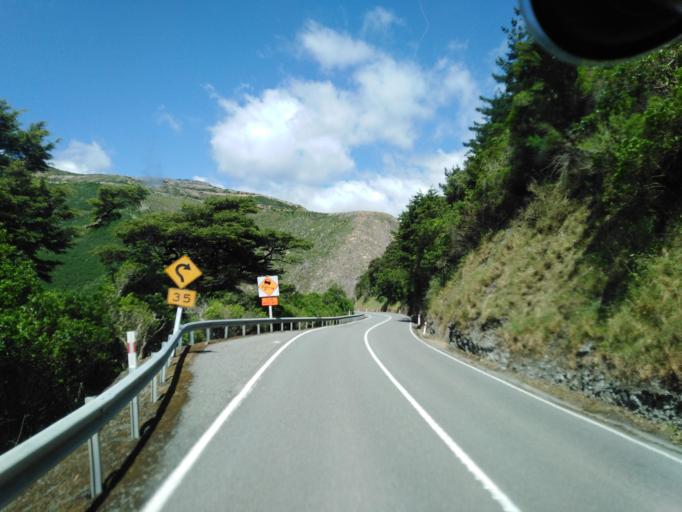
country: NZ
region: Nelson
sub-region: Nelson City
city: Nelson
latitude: -41.2294
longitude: 173.4152
